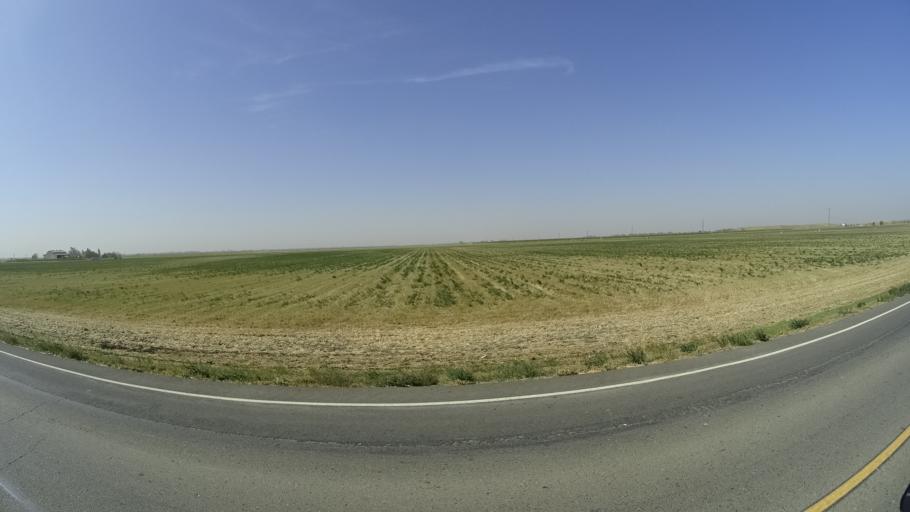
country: US
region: California
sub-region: Yolo County
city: Davis
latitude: 38.5807
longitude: -121.6750
